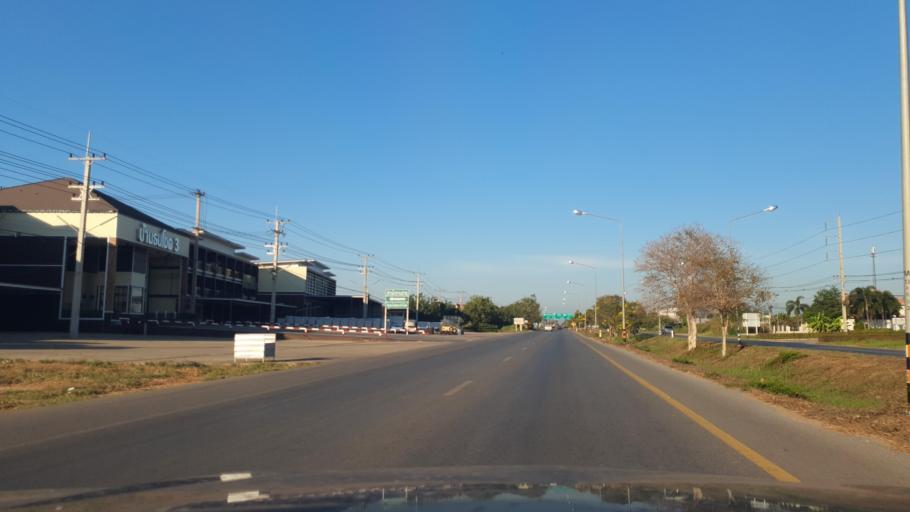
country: TH
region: Phitsanulok
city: Phitsanulok
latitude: 16.8647
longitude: 100.2543
